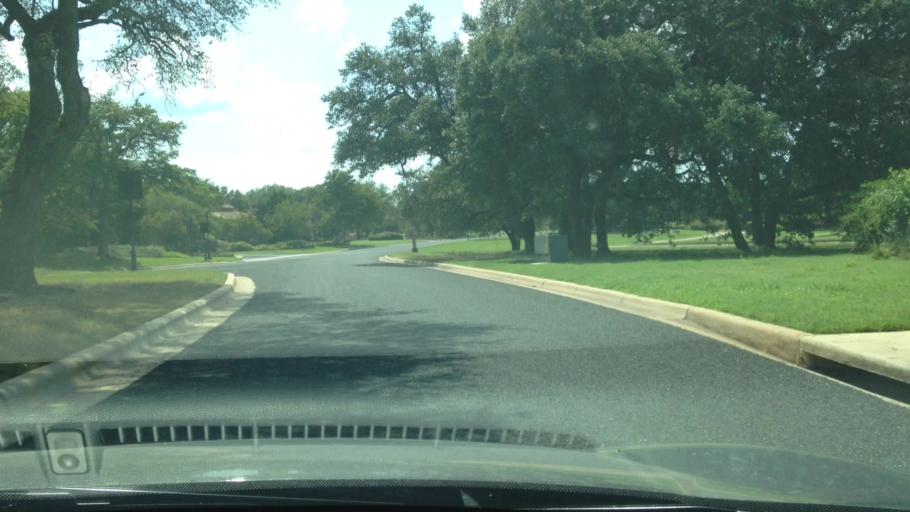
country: US
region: Texas
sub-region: Williamson County
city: Leander
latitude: 30.6380
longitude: -97.7917
